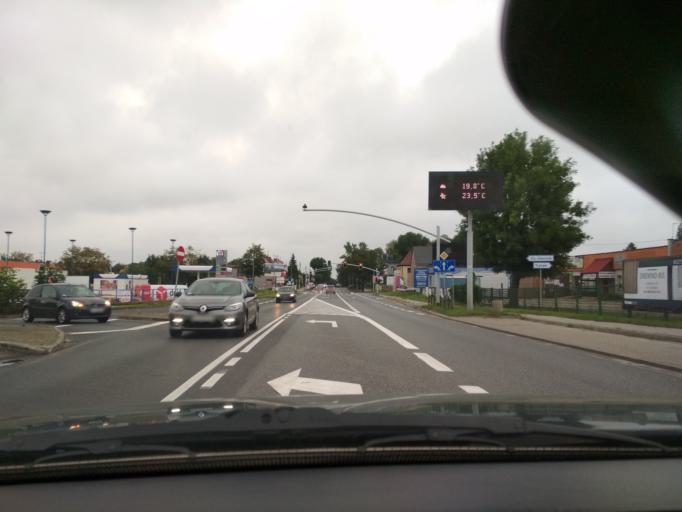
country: PL
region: Silesian Voivodeship
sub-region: Gliwice
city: Gliwice
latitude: 50.2754
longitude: 18.6614
